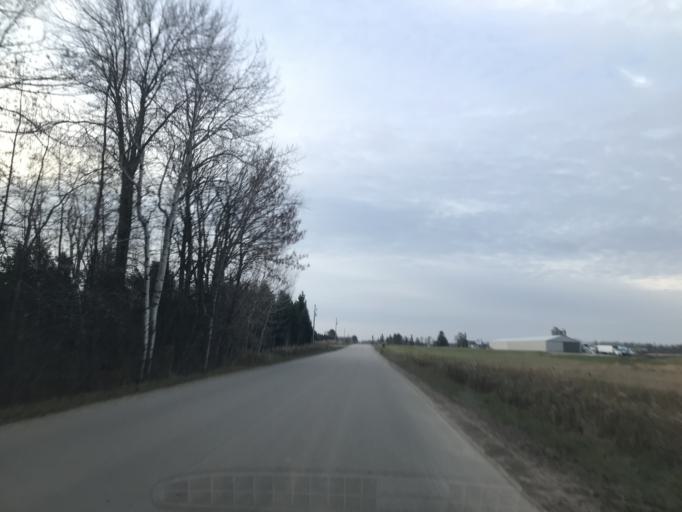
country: US
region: Wisconsin
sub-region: Marinette County
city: Peshtigo
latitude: 45.0867
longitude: -87.7995
